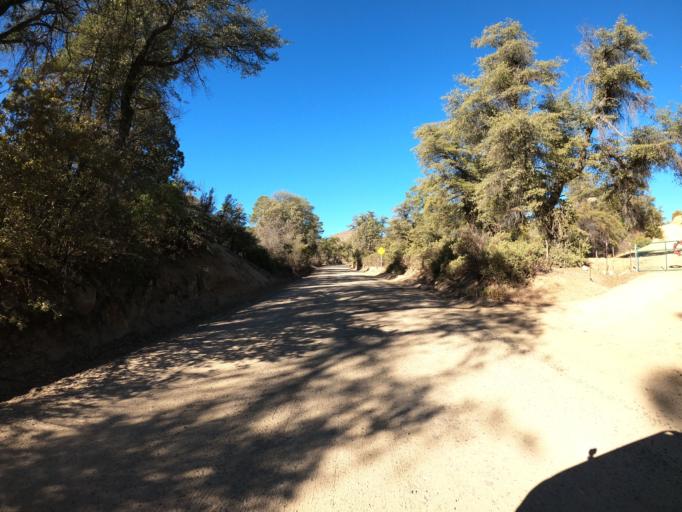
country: US
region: Arizona
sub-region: Yavapai County
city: Verde Village
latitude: 34.5878
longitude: -112.0498
